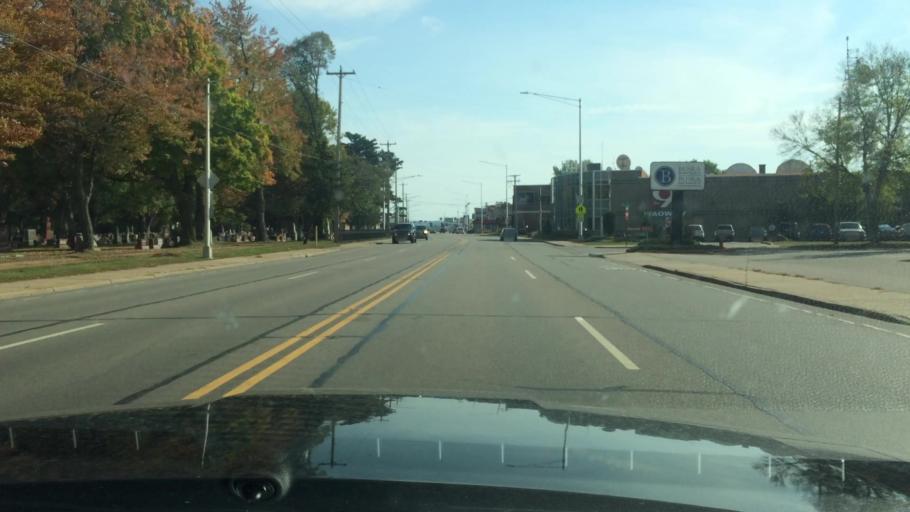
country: US
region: Wisconsin
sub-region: Marathon County
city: Wausau
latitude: 44.9385
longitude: -89.6182
